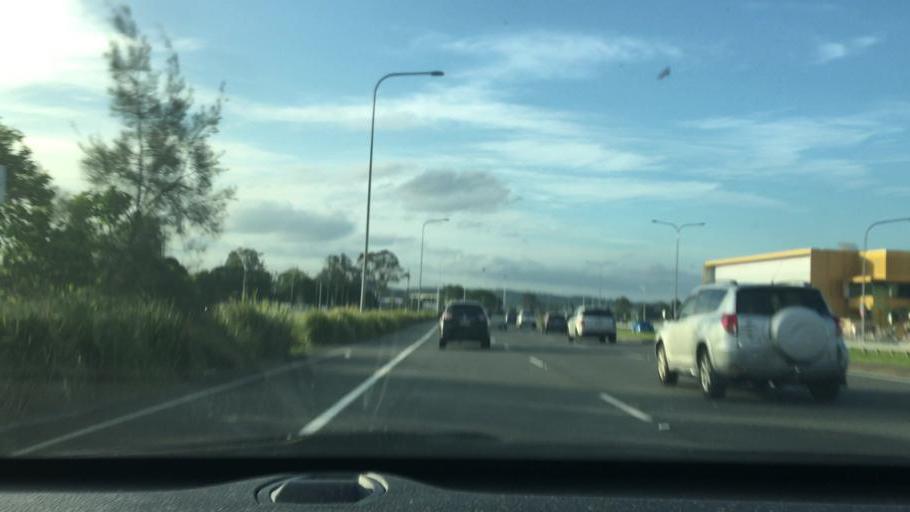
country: AU
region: Queensland
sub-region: Gold Coast
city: Nerang
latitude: -28.0068
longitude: 153.3644
